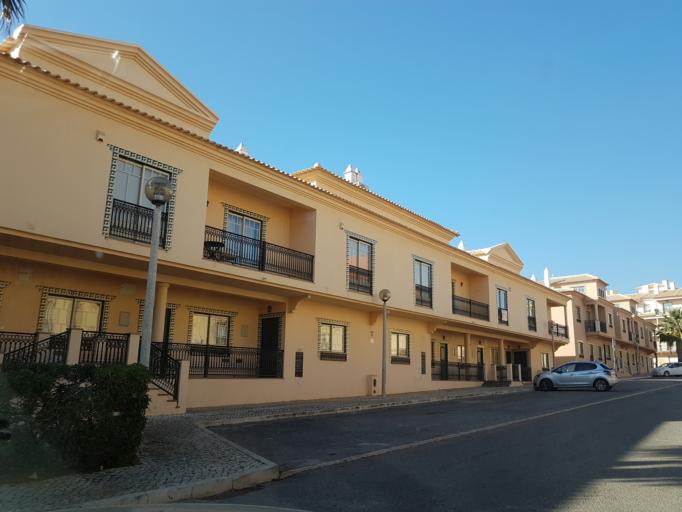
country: PT
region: Faro
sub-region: Albufeira
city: Albufeira
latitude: 37.0873
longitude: -8.2214
